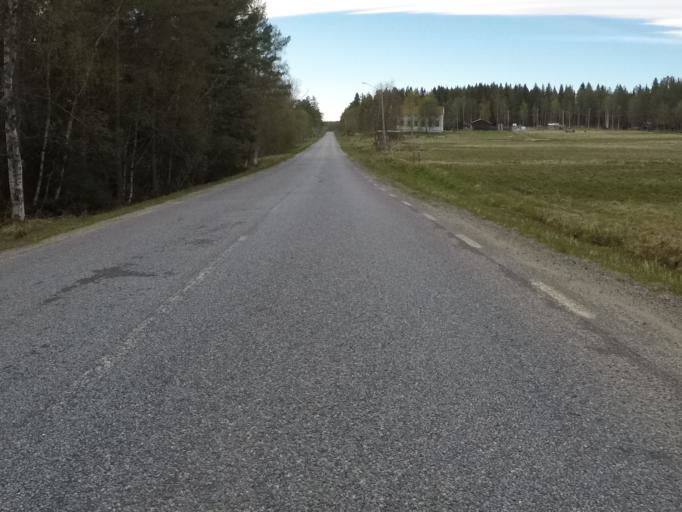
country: SE
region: Vaesterbotten
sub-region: Robertsfors Kommun
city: Robertsfors
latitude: 63.9909
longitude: 20.8109
